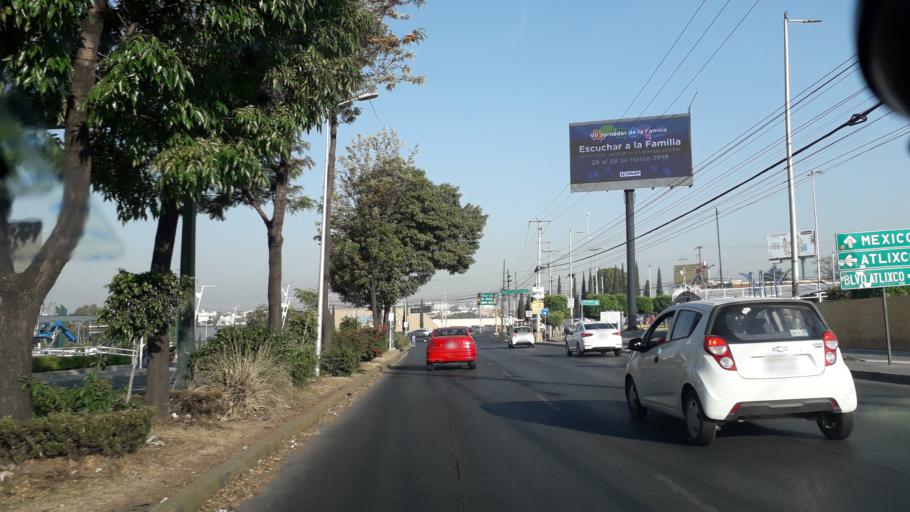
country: MX
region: Puebla
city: Puebla
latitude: 19.0440
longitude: -98.2347
